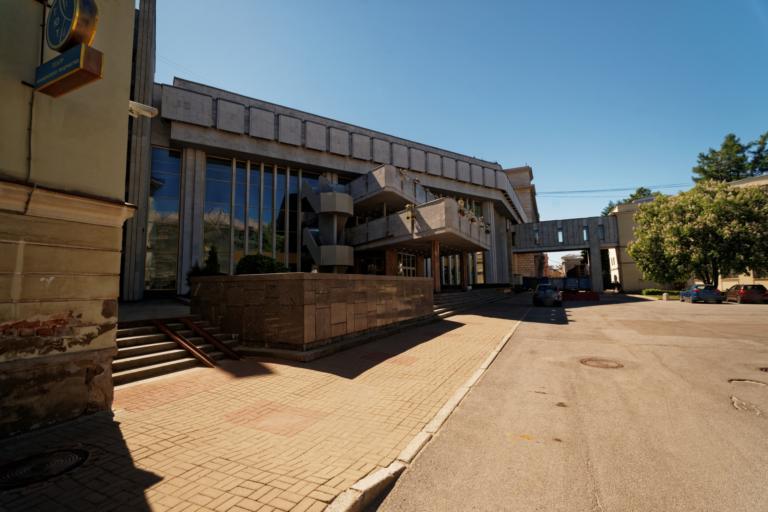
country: RU
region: St.-Petersburg
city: Centralniy
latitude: 59.9317
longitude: 30.3402
